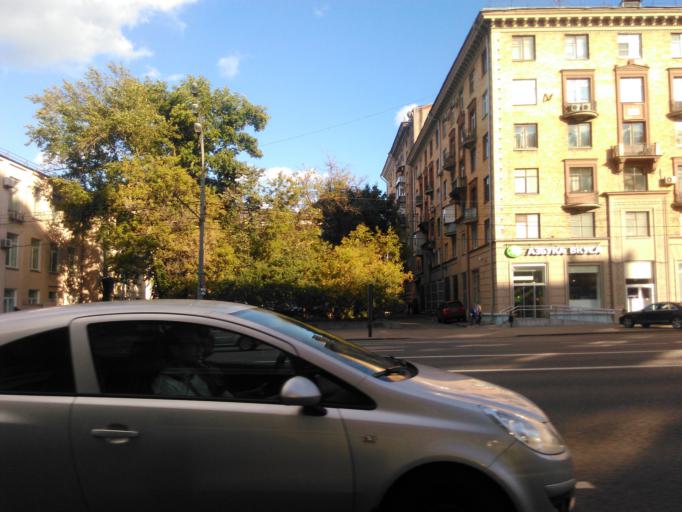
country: RU
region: Moscow
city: Novyye Cheremushki
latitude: 55.7186
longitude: 37.5963
